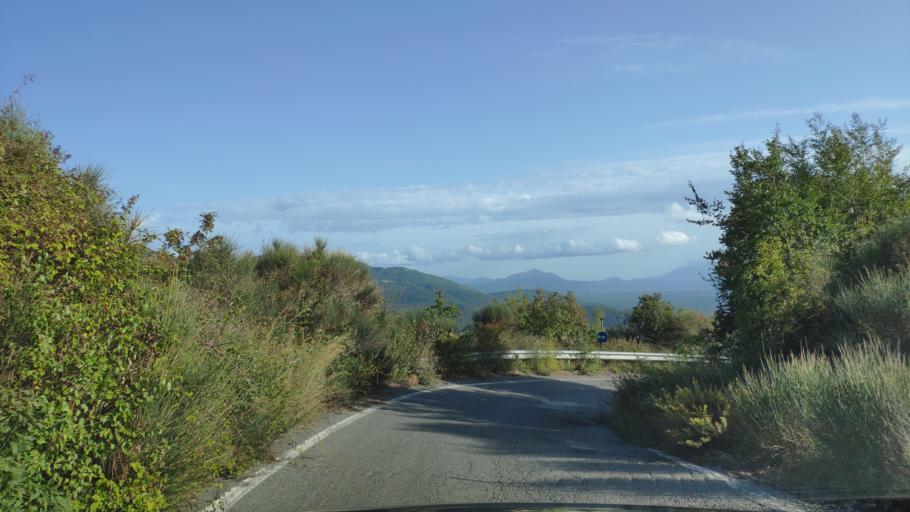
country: GR
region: Peloponnese
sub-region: Nomos Arkadias
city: Dimitsana
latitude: 37.5617
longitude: 22.0320
